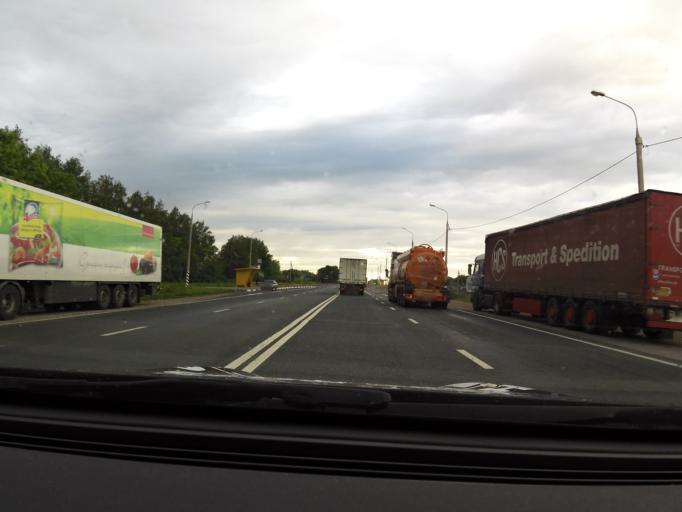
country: RU
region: Chuvashia
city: Yantikovo
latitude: 55.7983
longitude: 48.0594
